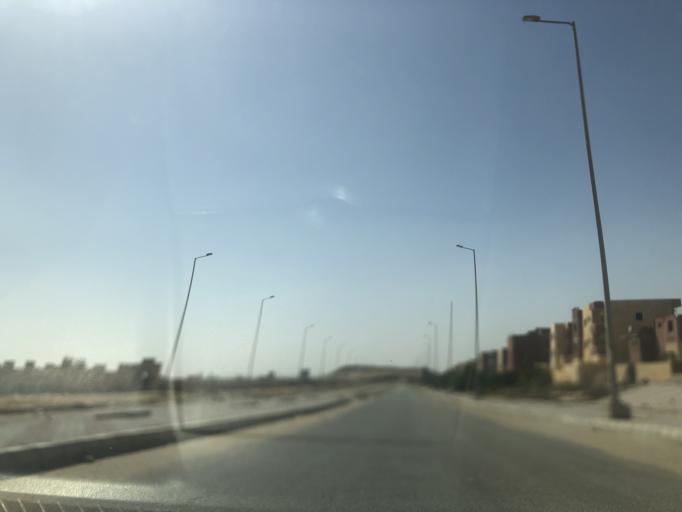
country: EG
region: Al Jizah
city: Madinat Sittah Uktubar
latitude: 29.9317
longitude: 30.9625
